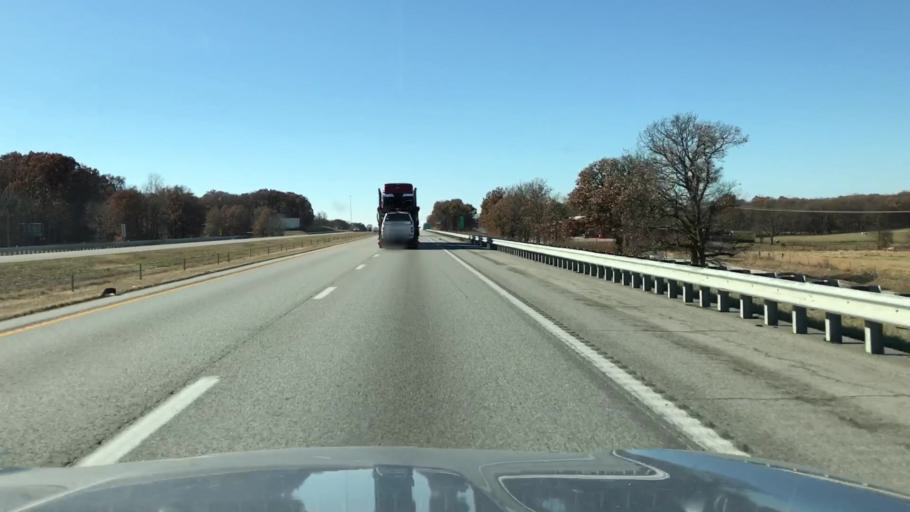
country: US
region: Missouri
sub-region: Jasper County
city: Duenweg
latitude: 37.0822
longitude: -94.3347
